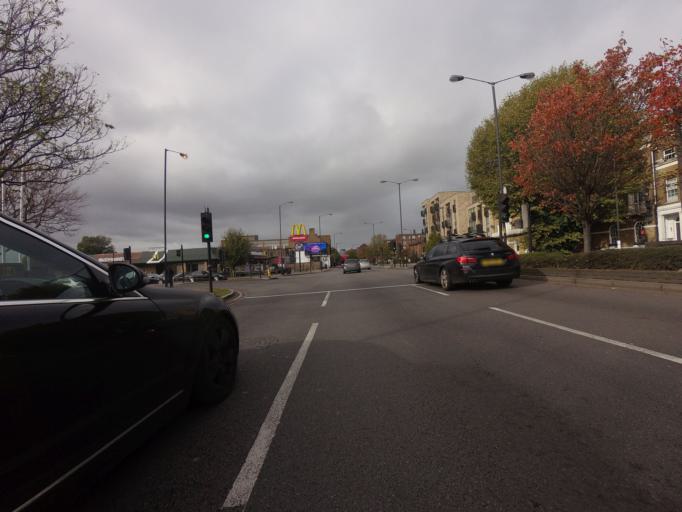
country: GB
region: England
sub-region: Greater London
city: Camberwell
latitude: 51.4845
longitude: -0.0675
